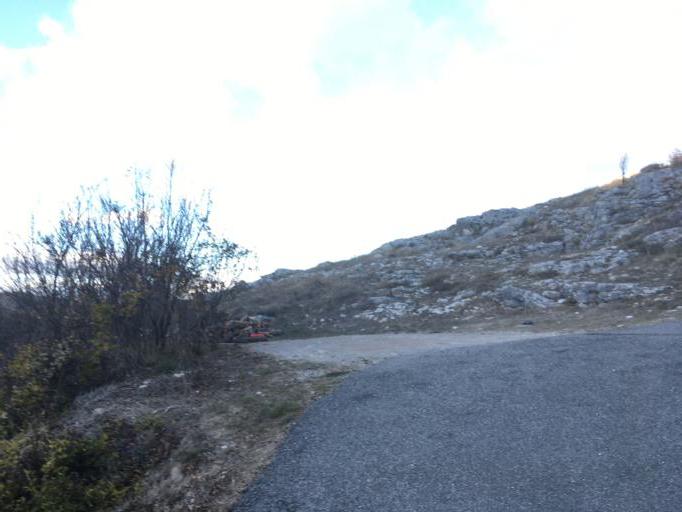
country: FR
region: Provence-Alpes-Cote d'Azur
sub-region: Departement du Var
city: Bargemon
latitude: 43.7105
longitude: 6.5102
